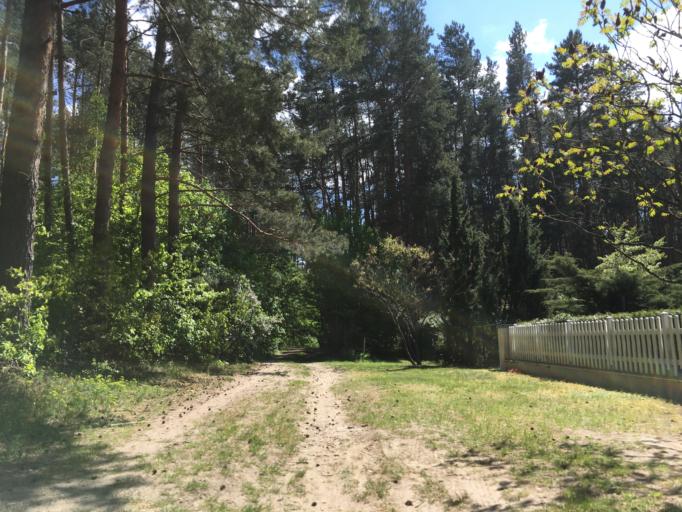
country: DE
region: Brandenburg
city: Rudnitz
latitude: 52.7205
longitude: 13.6581
